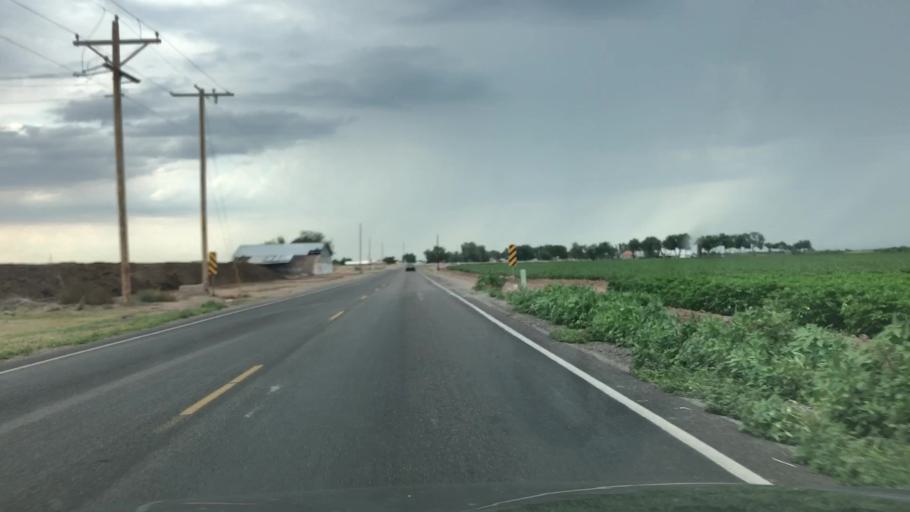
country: US
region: New Mexico
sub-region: Dona Ana County
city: Anthony
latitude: 32.0225
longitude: -106.6705
